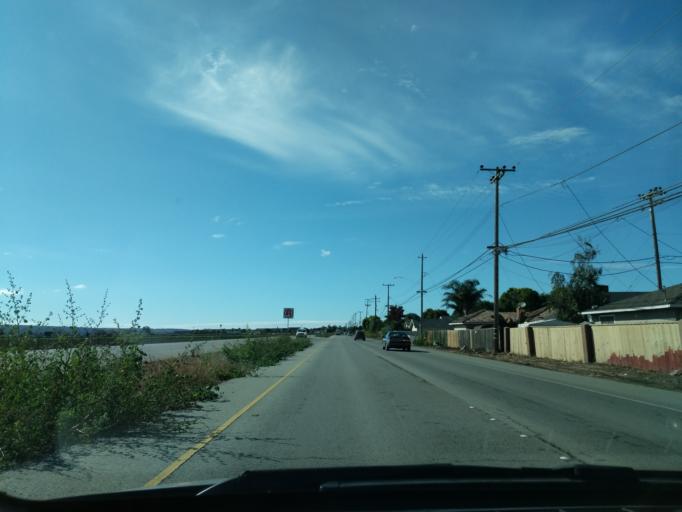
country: US
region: California
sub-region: Monterey County
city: Salinas
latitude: 36.6537
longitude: -121.6514
